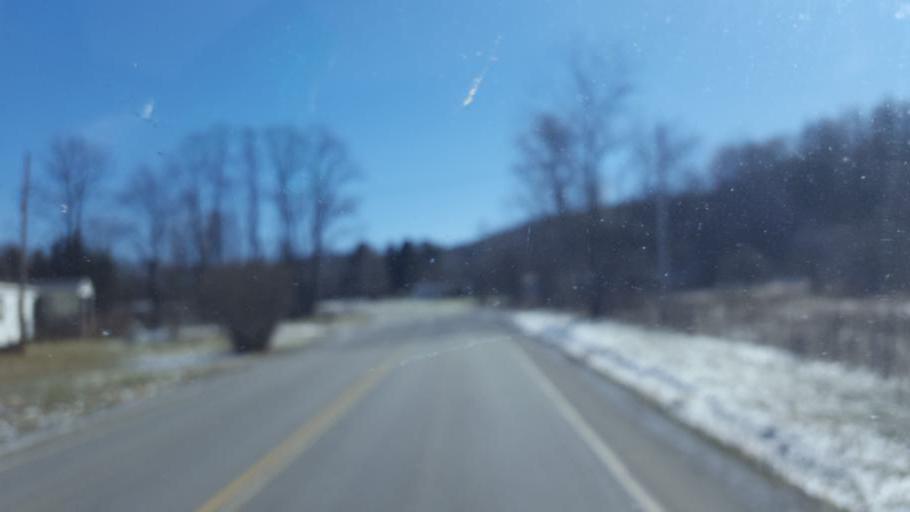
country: US
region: New York
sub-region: Allegany County
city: Wellsville
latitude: 42.0763
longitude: -77.8996
